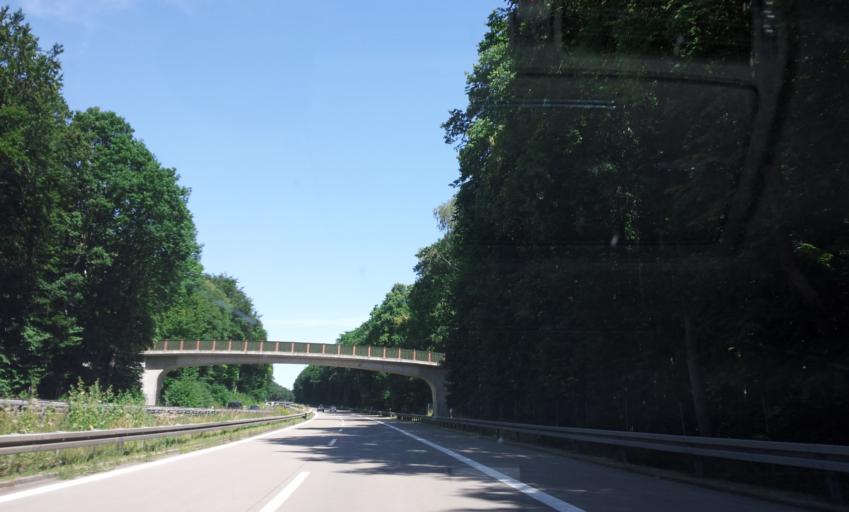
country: DE
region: Brandenburg
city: Gramzow
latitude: 53.1438
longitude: 13.8961
